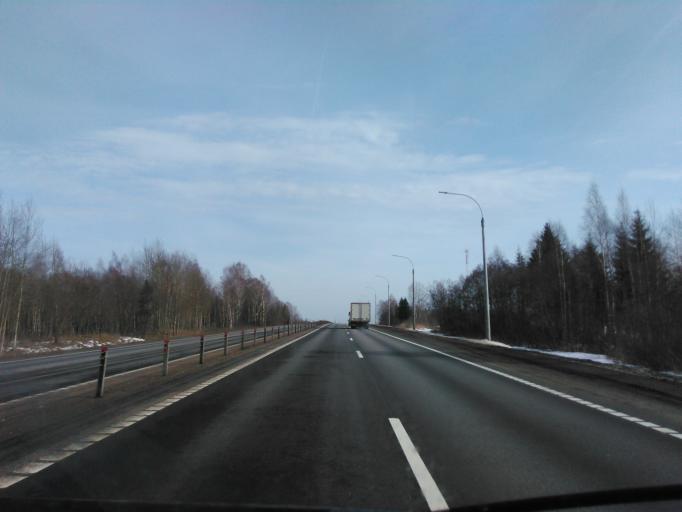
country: BY
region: Vitebsk
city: Dubrowna
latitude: 54.6889
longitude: 30.8796
